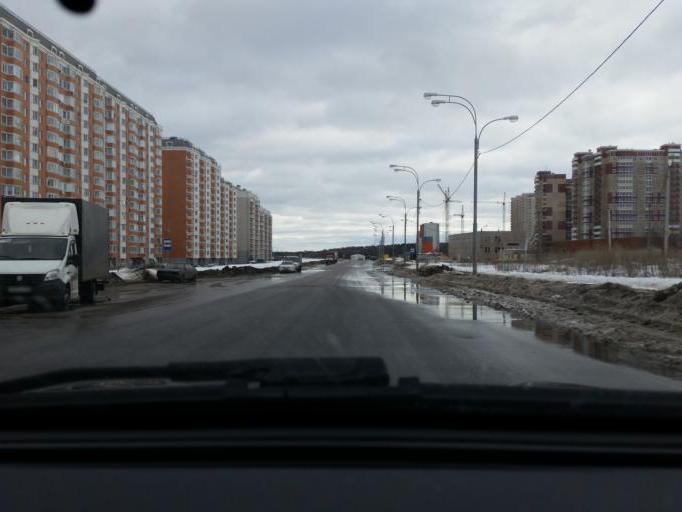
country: RU
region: Moskovskaya
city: Shcherbinka
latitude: 55.5272
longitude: 37.5856
